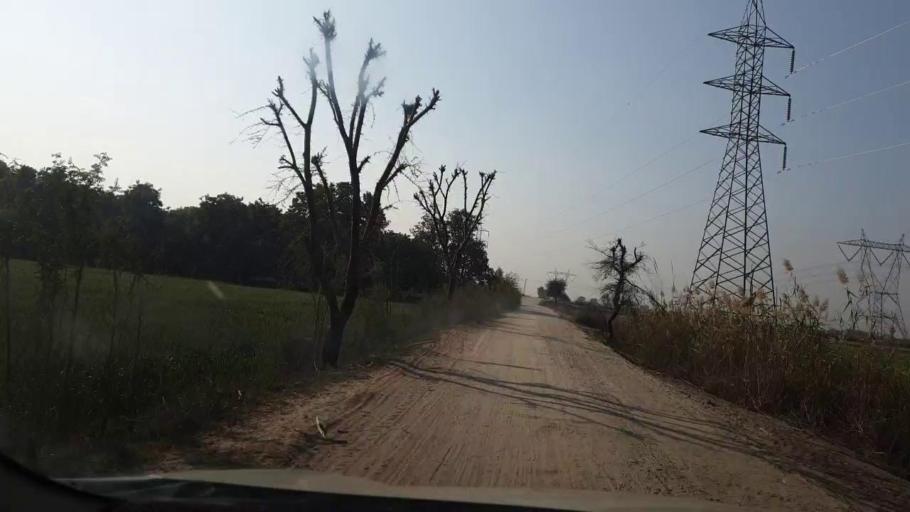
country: PK
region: Sindh
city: Bhit Shah
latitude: 25.6900
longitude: 68.5422
